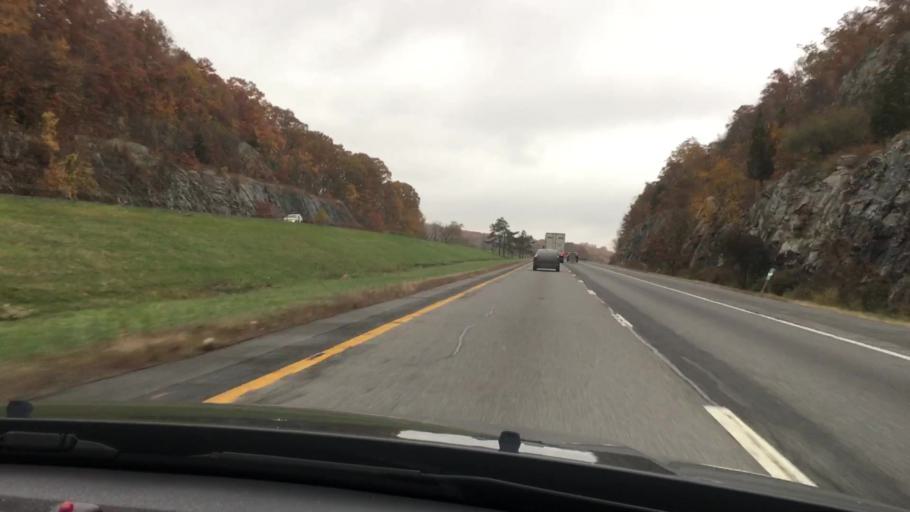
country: US
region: New York
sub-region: Putnam County
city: Lake Carmel
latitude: 41.4540
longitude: -73.6396
